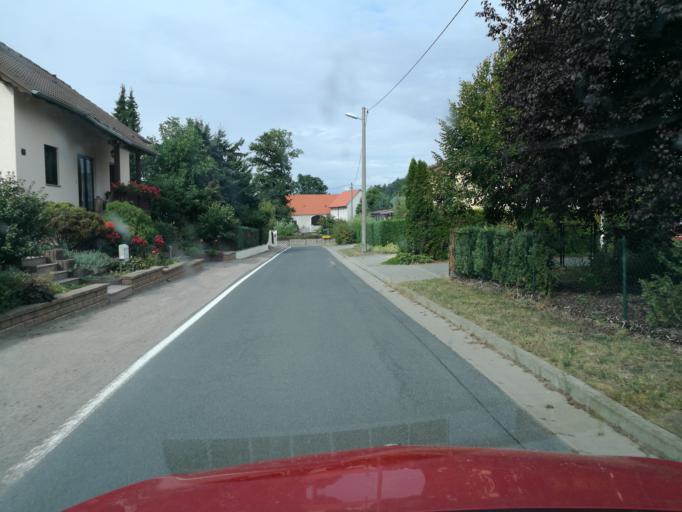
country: DE
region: Saxony
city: Oschatz
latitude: 51.2809
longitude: 13.0826
